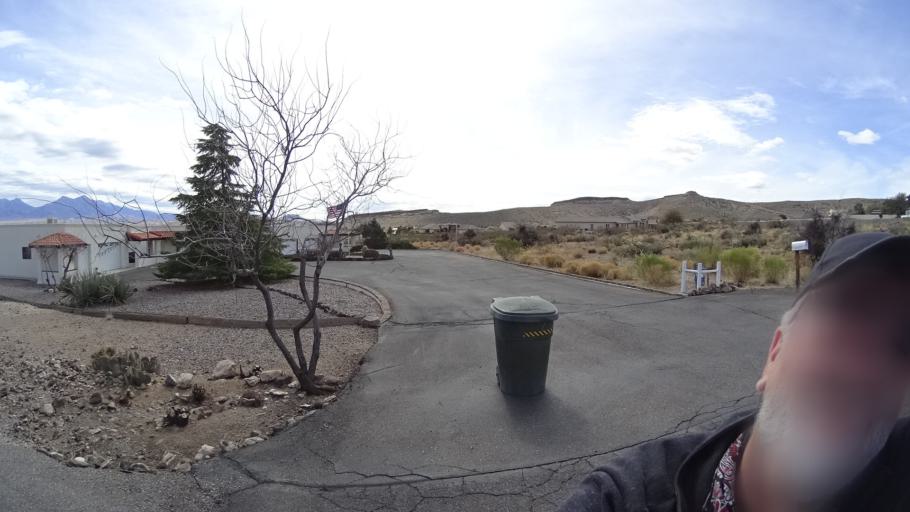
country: US
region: Arizona
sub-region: Mohave County
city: New Kingman-Butler
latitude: 35.2357
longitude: -114.0501
